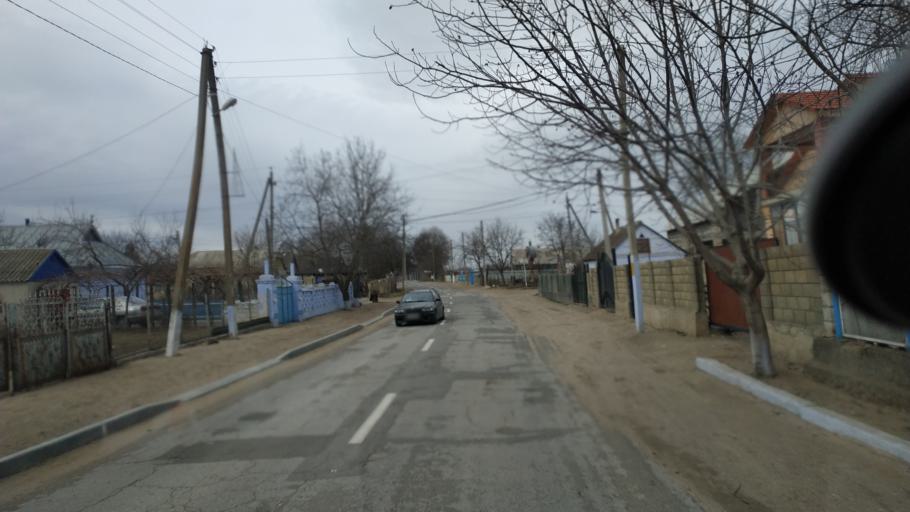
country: MD
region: Telenesti
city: Cocieri
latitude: 47.3165
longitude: 29.1038
